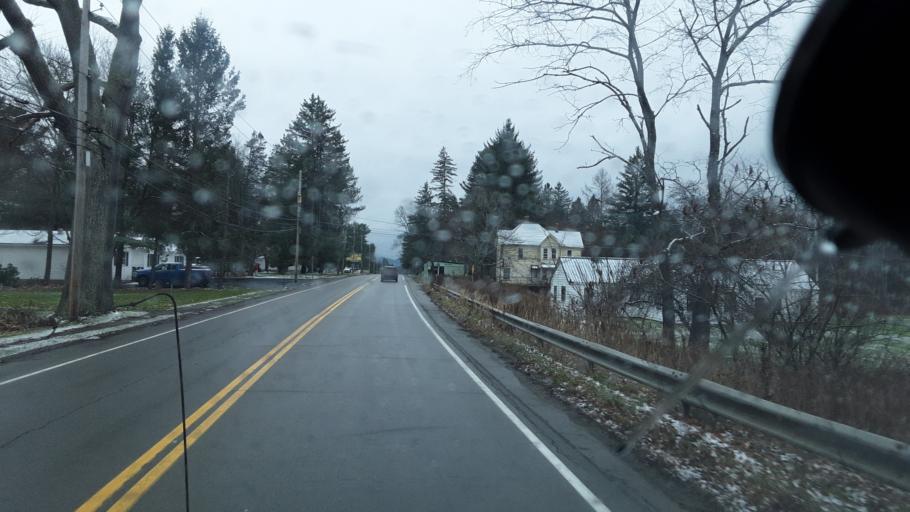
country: US
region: New York
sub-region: Cattaraugus County
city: Westons Mills
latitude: 42.0611
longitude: -78.3755
